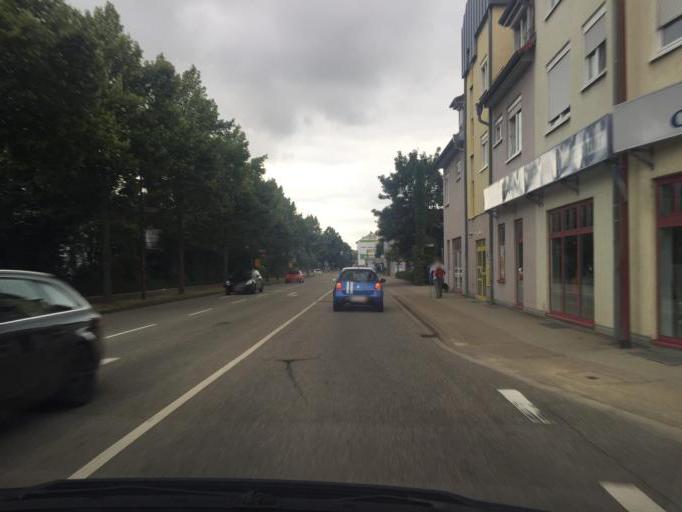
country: DE
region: Baden-Wuerttemberg
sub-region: Karlsruhe Region
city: Bretten
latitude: 49.0332
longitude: 8.7058
